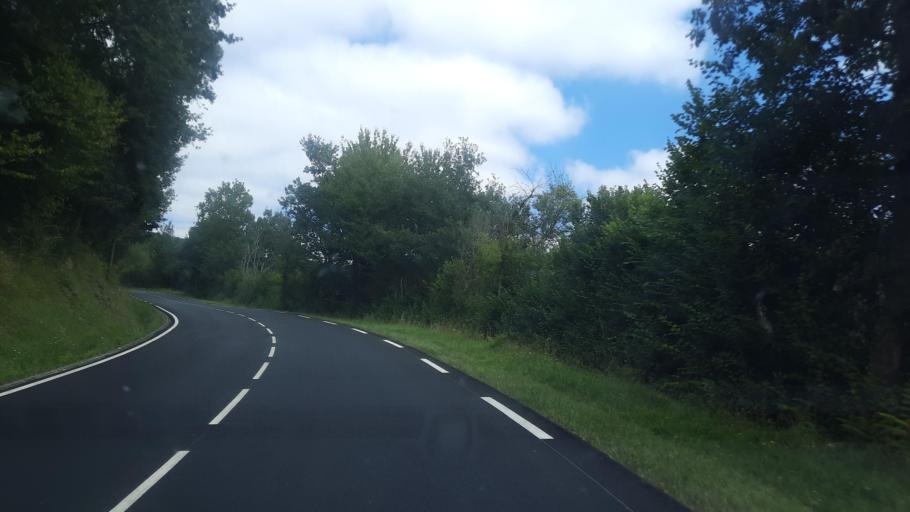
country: FR
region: Midi-Pyrenees
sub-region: Departement de la Haute-Garonne
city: Boulogne-sur-Gesse
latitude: 43.2866
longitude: 0.5495
